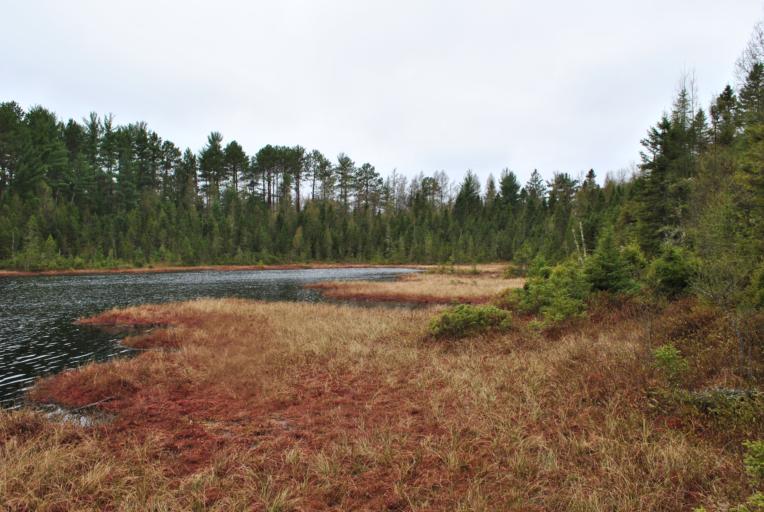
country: US
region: Wisconsin
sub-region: Vilas County
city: Eagle River
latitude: 45.9534
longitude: -89.3593
